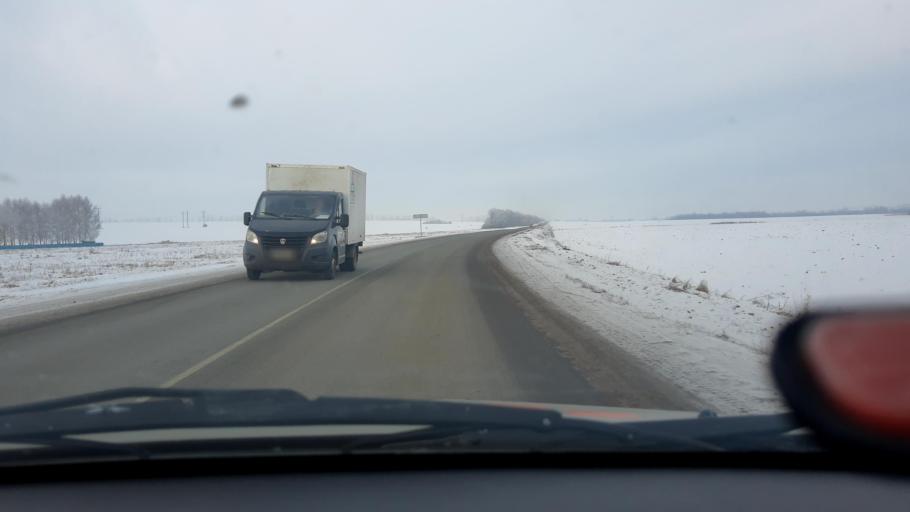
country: RU
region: Bashkortostan
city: Avdon
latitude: 54.3841
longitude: 55.8057
